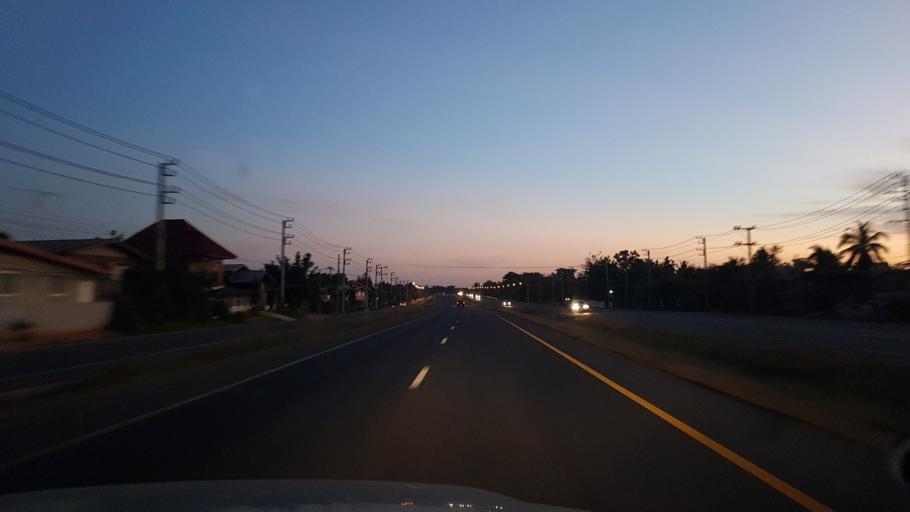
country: TH
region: Chaiyaphum
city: Phu Khiao
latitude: 16.2964
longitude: 102.2098
